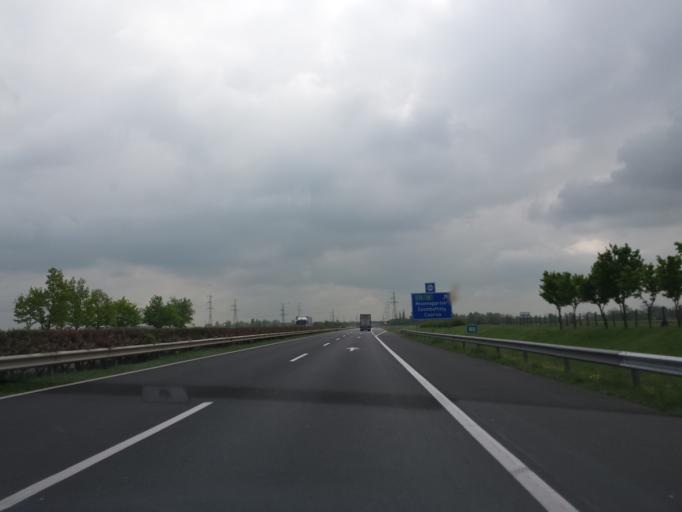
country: HU
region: Gyor-Moson-Sopron
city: Mosonmagyarovar
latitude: 47.8576
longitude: 17.2403
